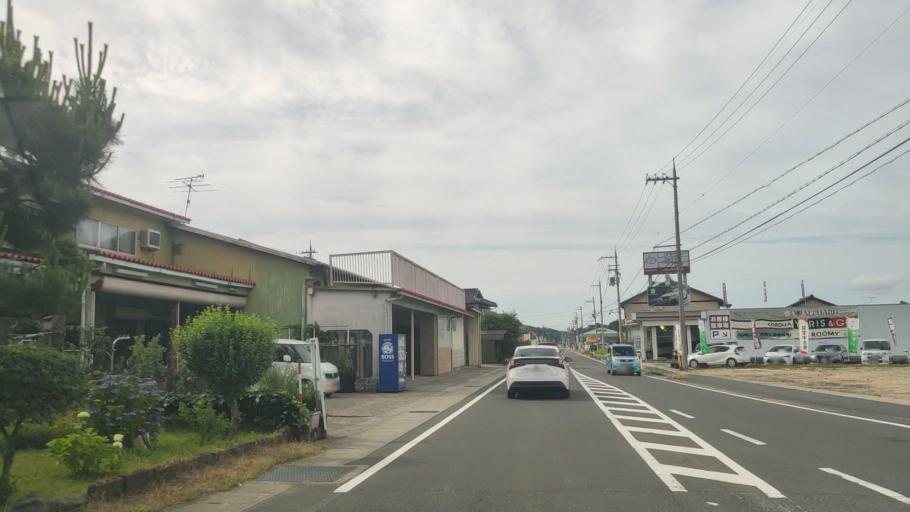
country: JP
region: Kyoto
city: Miyazu
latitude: 35.6202
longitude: 135.0746
